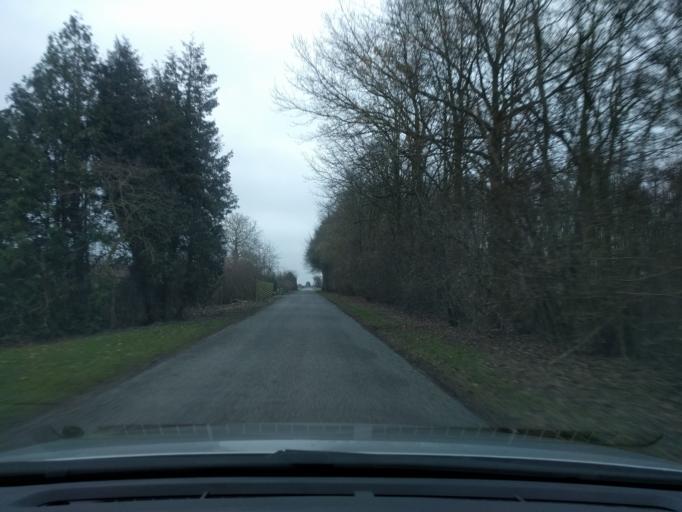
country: DK
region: South Denmark
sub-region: Odense Kommune
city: Neder Holluf
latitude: 55.3805
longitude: 10.4964
